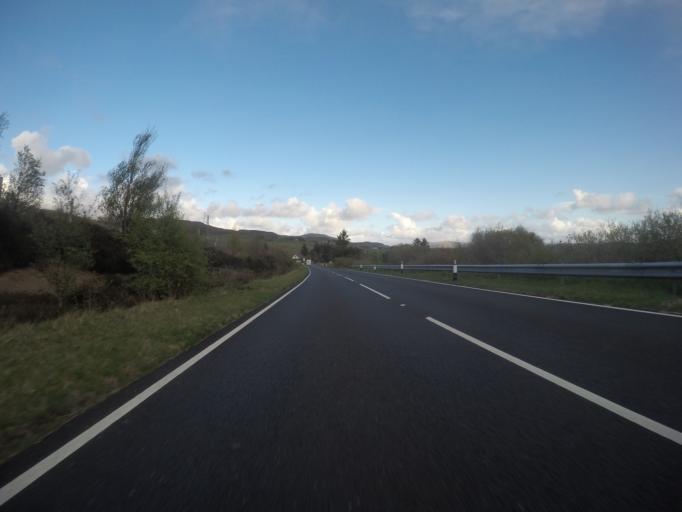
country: GB
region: Scotland
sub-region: Highland
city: Portree
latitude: 57.5003
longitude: -6.3273
